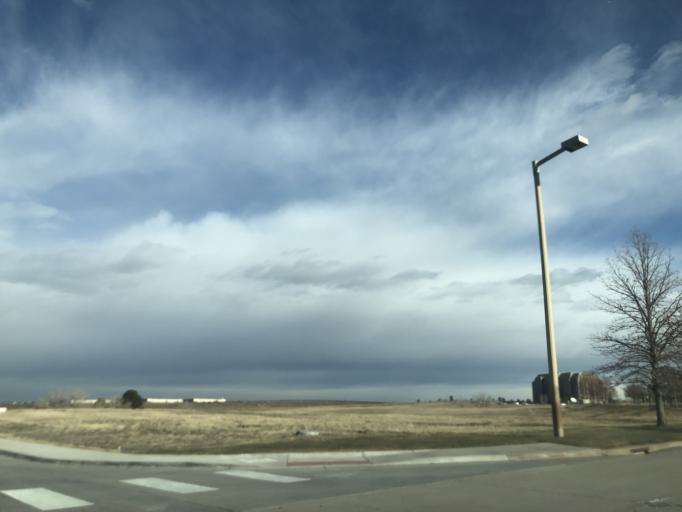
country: US
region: Colorado
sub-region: Douglas County
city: Meridian
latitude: 39.5477
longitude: -104.8615
